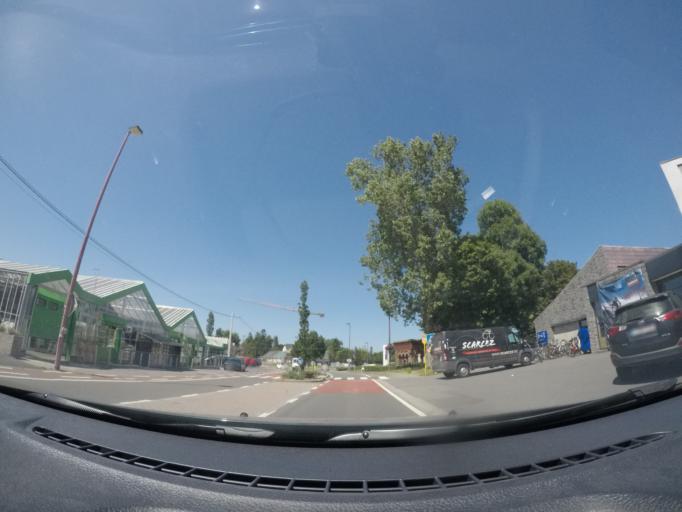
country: BE
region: Wallonia
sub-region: Province de Namur
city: Beauraing
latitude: 50.1193
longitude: 4.9552
